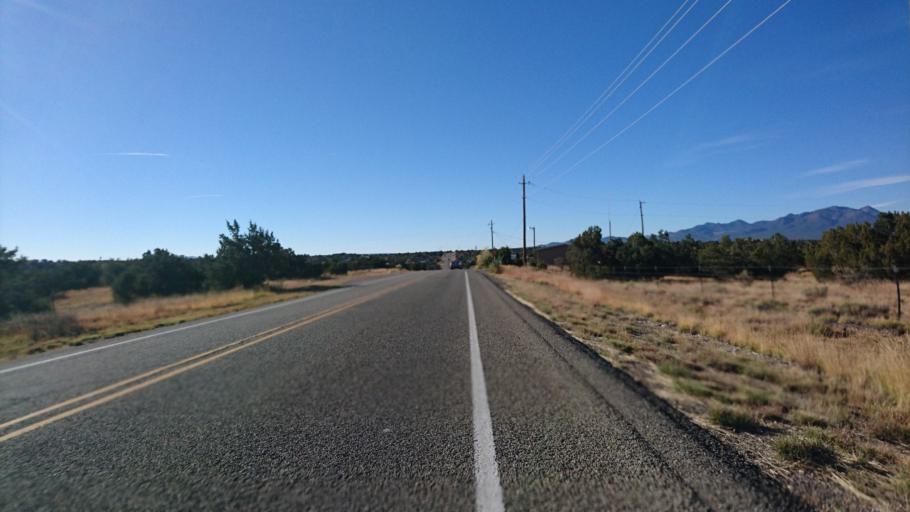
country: US
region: New Mexico
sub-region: Santa Fe County
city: La Cienega
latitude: 35.4631
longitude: -106.0702
